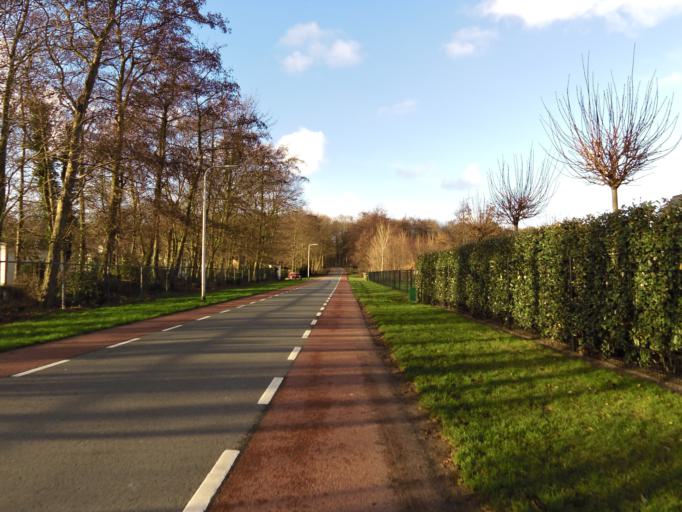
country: NL
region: South Holland
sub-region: Gemeente Noordwijkerhout
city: Noordwijkerhout
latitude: 52.2745
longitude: 4.4771
